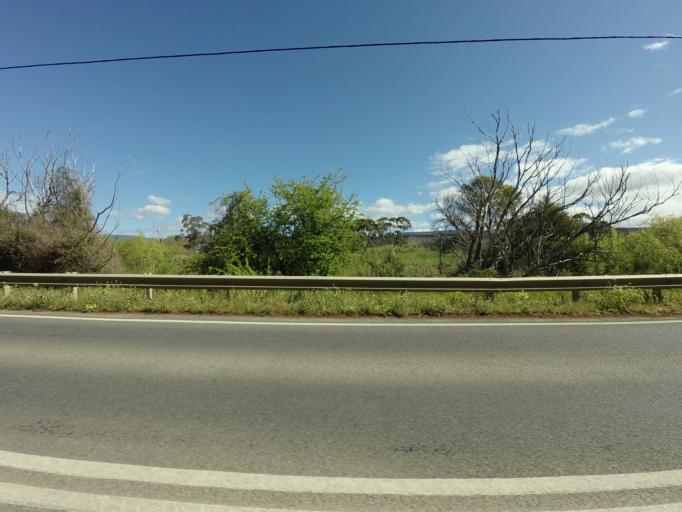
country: AU
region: Tasmania
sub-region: Derwent Valley
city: New Norfolk
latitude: -42.7403
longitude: 146.9819
